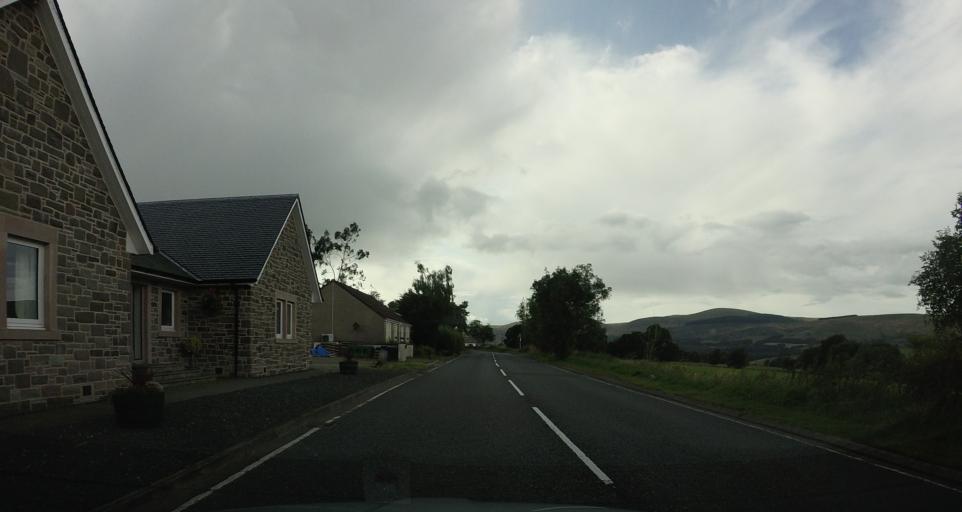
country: GB
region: Scotland
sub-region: Fife
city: Saline
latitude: 56.1620
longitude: -3.5906
